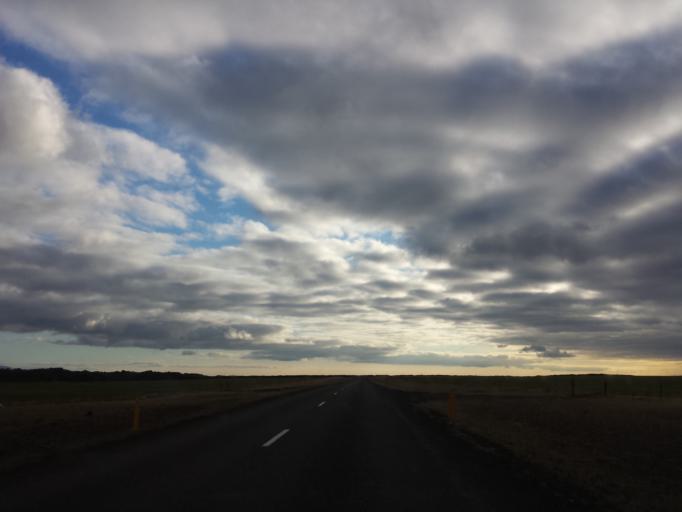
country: IS
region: West
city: Borgarnes
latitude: 64.7753
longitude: -22.2669
